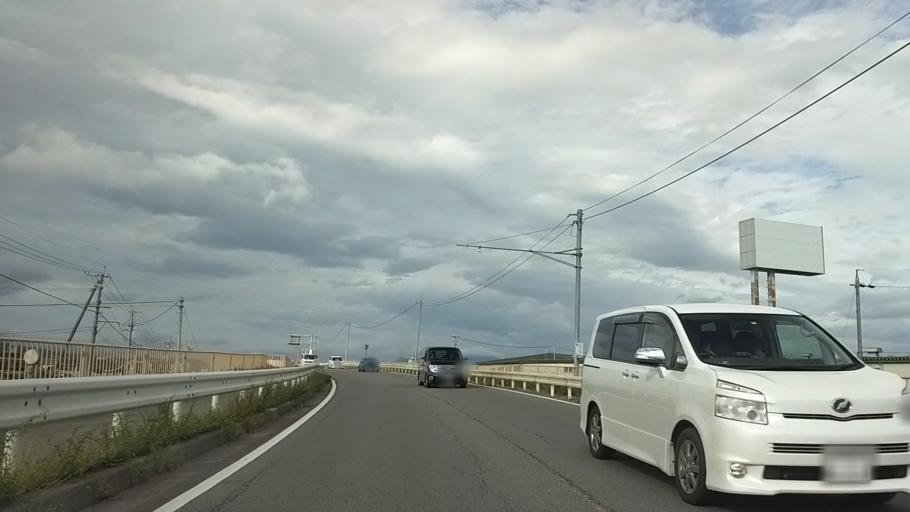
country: JP
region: Nagano
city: Suzaka
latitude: 36.6627
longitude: 138.2614
